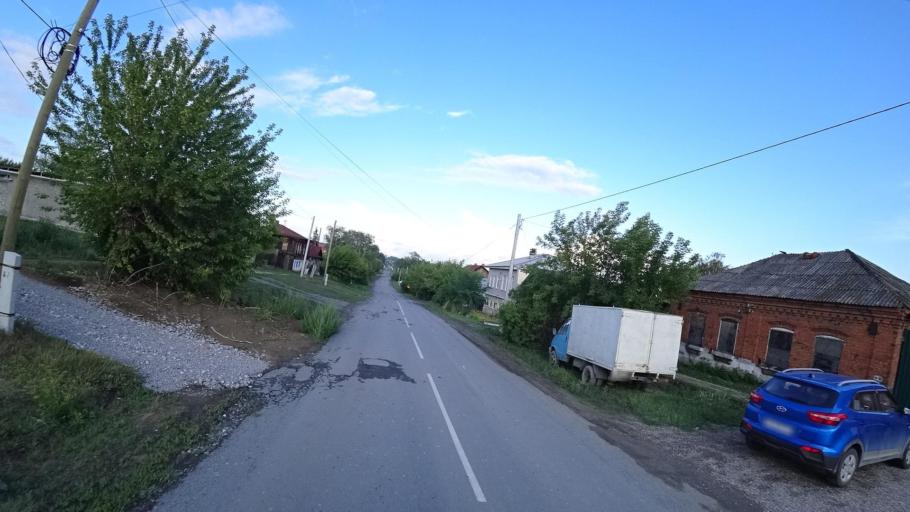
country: RU
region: Sverdlovsk
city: Kamyshlov
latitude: 56.8490
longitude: 62.7029
